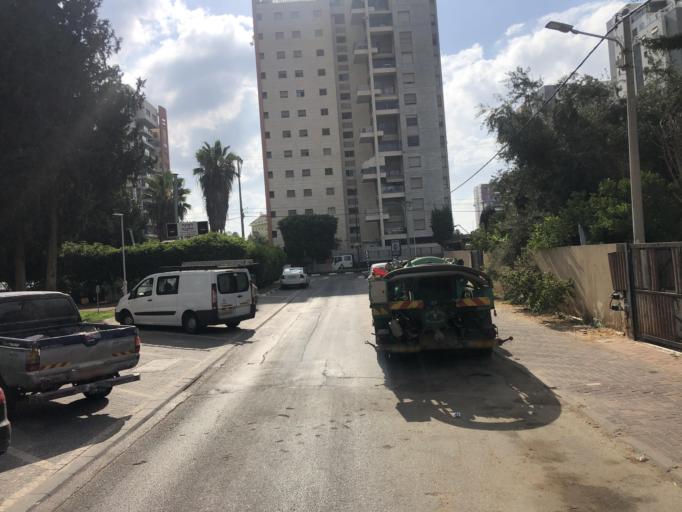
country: IL
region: Central District
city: Yehud
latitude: 32.0301
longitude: 34.8852
